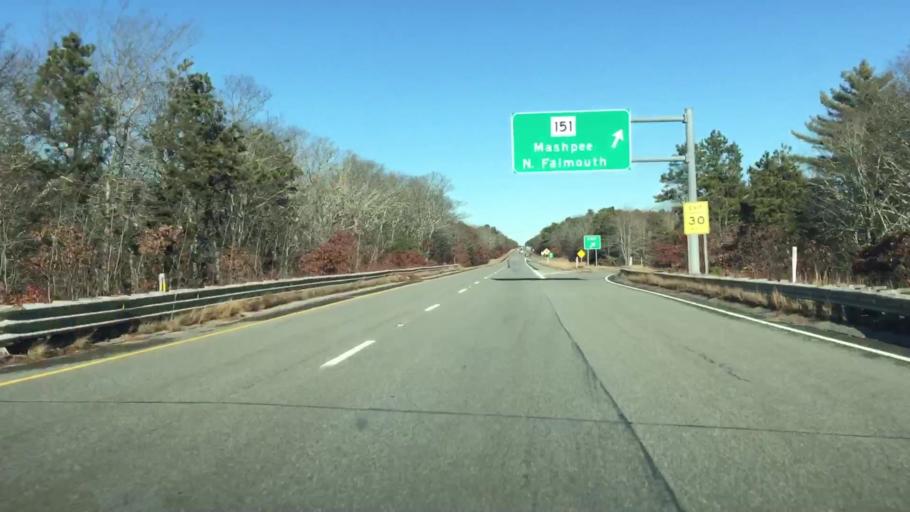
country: US
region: Massachusetts
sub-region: Barnstable County
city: North Falmouth
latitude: 41.6449
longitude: -70.6045
